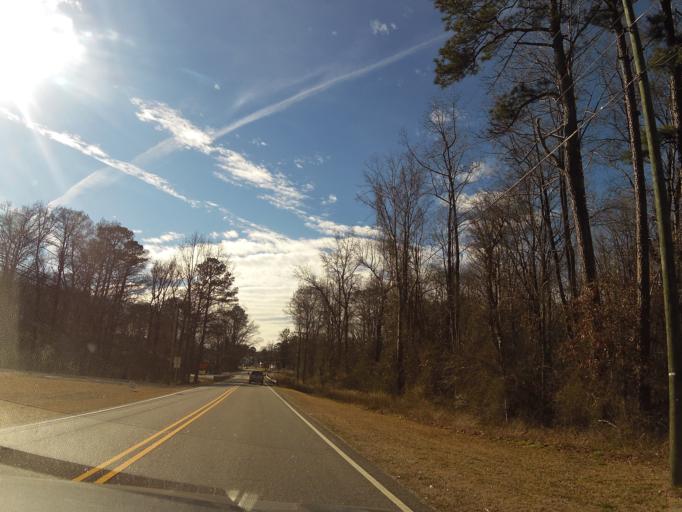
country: US
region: Virginia
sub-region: Isle of Wight County
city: Windsor
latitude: 36.7757
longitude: -76.8442
